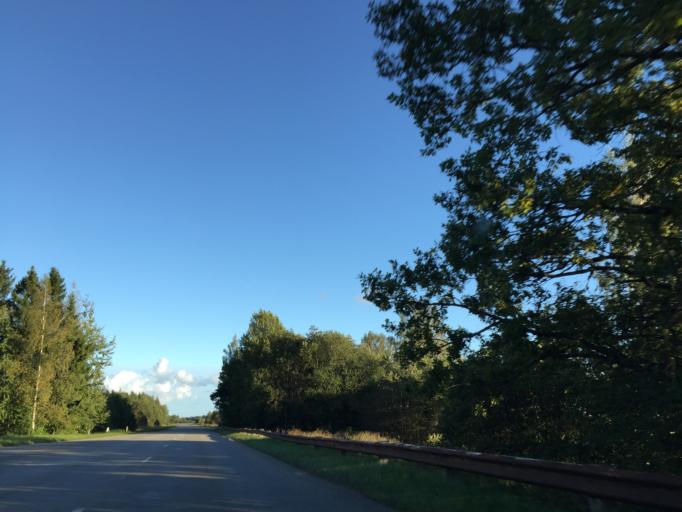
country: LV
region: Kuldigas Rajons
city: Kuldiga
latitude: 56.9422
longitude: 22.0227
